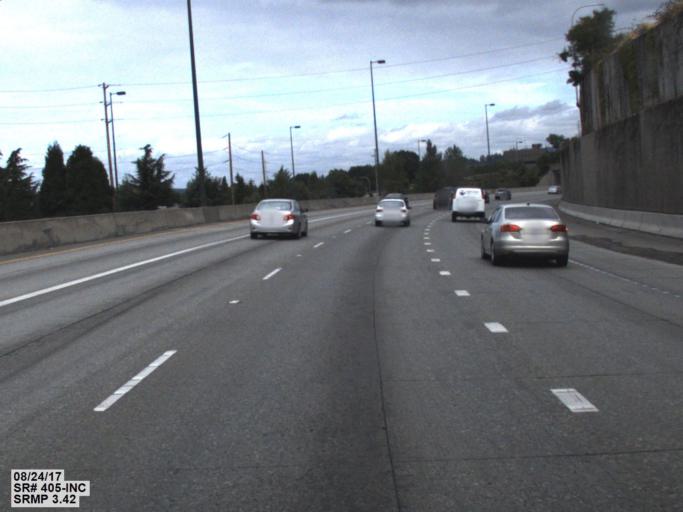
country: US
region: Washington
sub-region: King County
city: Renton
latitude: 47.4770
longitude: -122.2034
